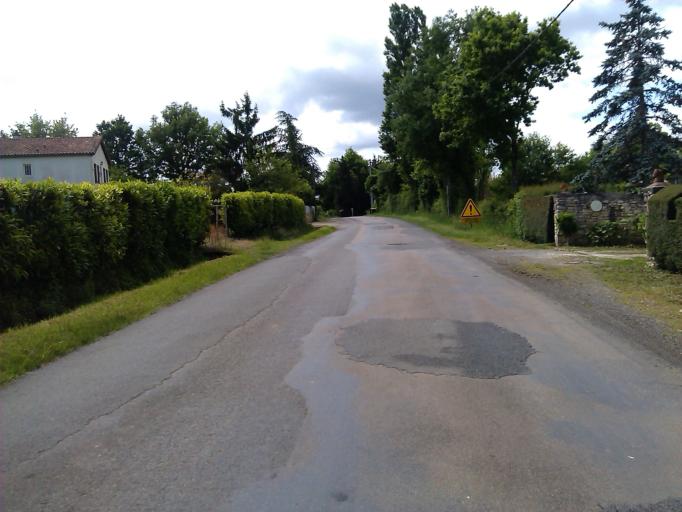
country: FR
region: Poitou-Charentes
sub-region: Departement de la Charente
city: Champagne-Mouton
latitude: 46.0335
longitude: 0.4491
